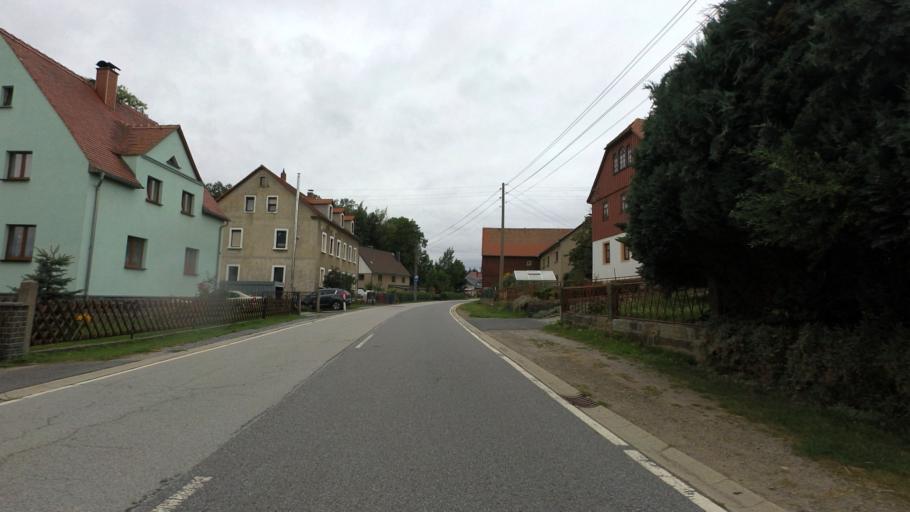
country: DE
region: Saxony
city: Berthelsdorf
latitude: 51.0685
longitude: 14.2068
